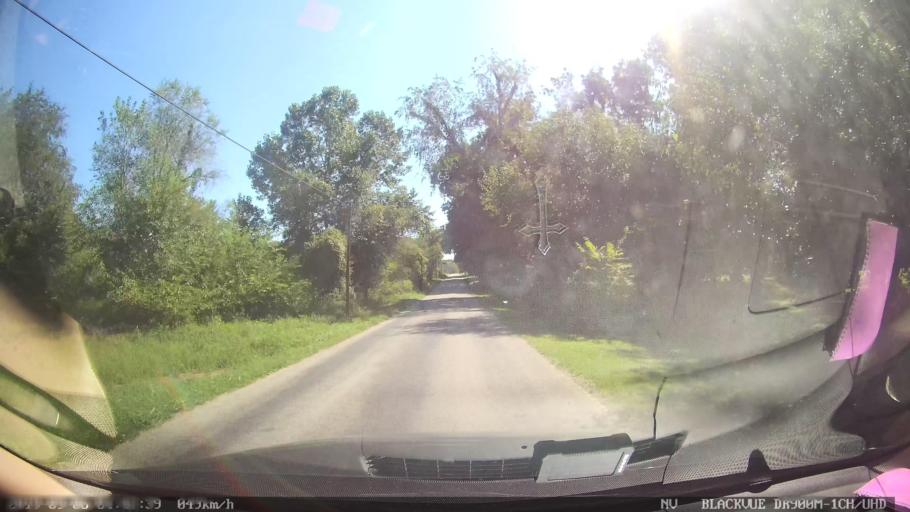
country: US
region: Ohio
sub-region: Licking County
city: Newark
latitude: 40.1220
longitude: -82.3833
